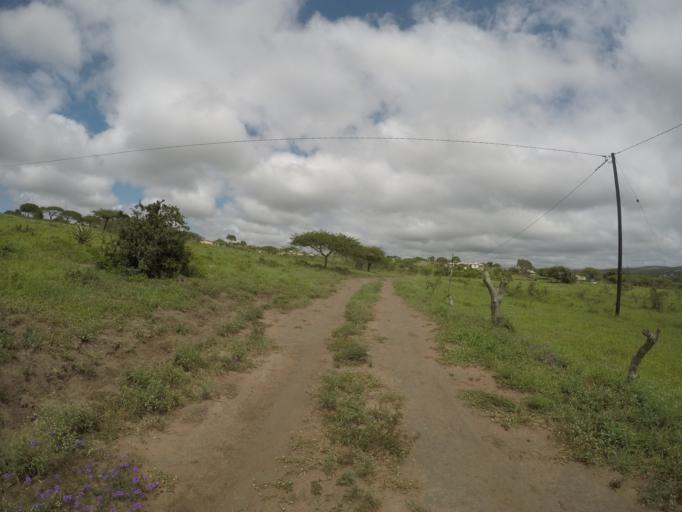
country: ZA
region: KwaZulu-Natal
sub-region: uThungulu District Municipality
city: Empangeni
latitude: -28.5718
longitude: 31.8436
